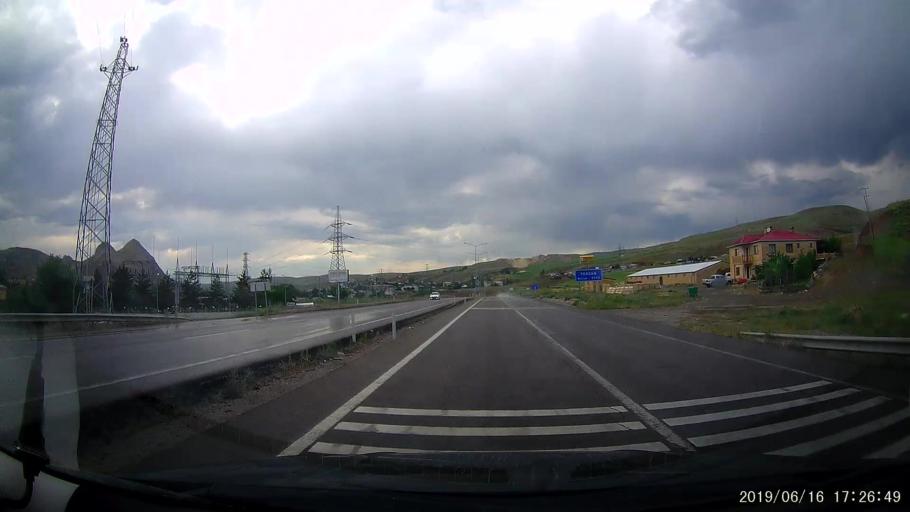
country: TR
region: Erzincan
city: Tercan
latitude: 39.7723
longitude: 40.4044
